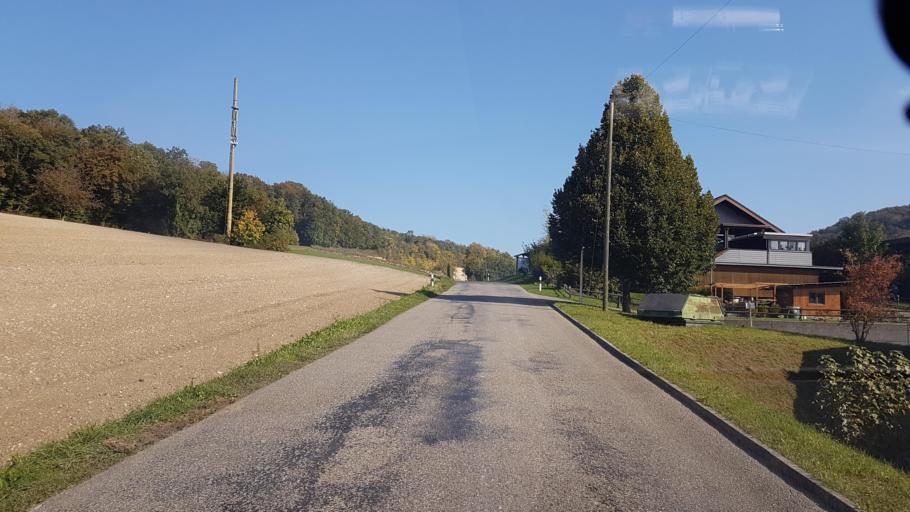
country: CH
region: Aargau
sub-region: Bezirk Laufenburg
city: Sulz
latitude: 47.5199
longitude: 8.1403
